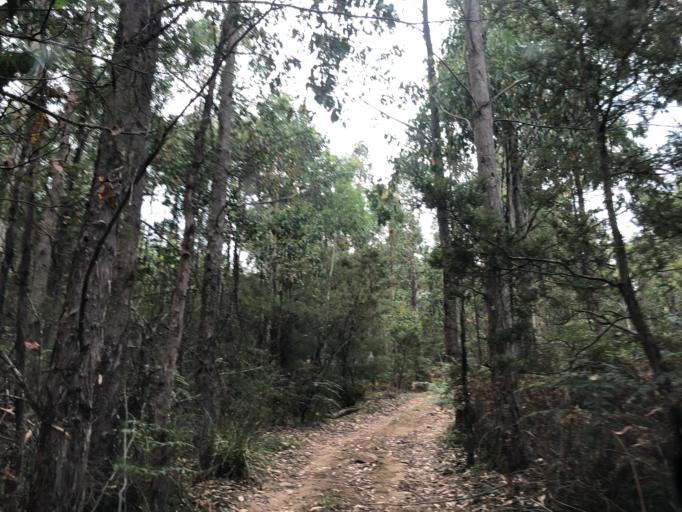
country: AU
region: Victoria
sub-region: Moorabool
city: Bacchus Marsh
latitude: -37.4463
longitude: 144.2433
